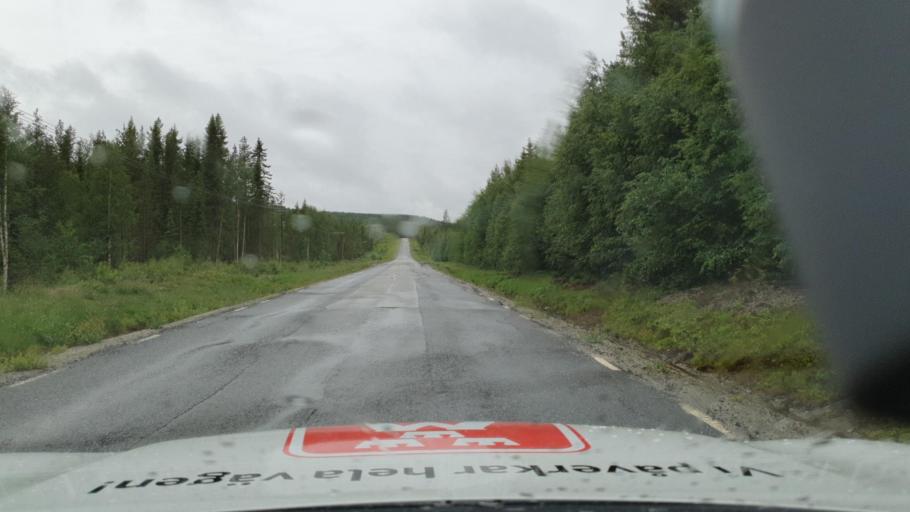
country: SE
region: Vaesterbotten
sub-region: Asele Kommun
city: Asele
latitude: 64.0078
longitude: 17.2387
